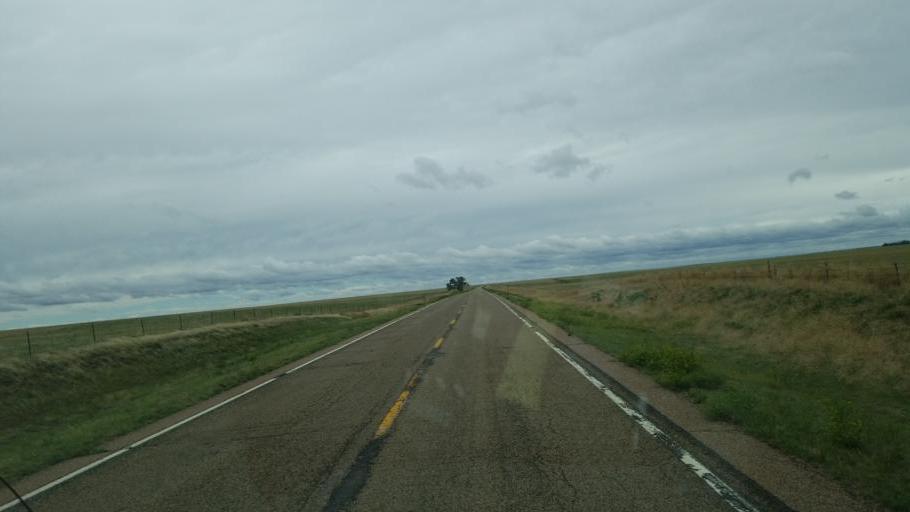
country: US
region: Colorado
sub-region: Lincoln County
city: Hugo
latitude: 38.8522
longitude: -103.7267
